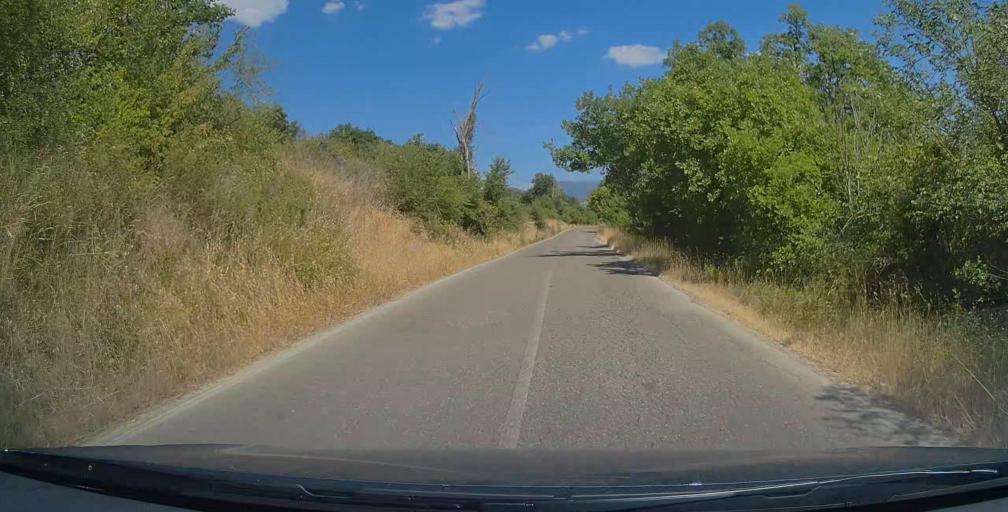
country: IT
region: Umbria
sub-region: Provincia di Terni
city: Otricoli
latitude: 42.3983
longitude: 12.4763
